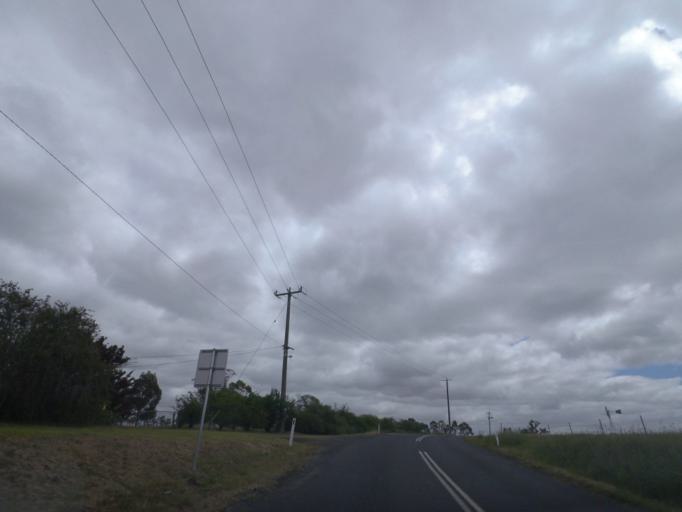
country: AU
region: Victoria
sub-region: Whittlesea
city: Whittlesea
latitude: -37.1879
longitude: 145.0382
